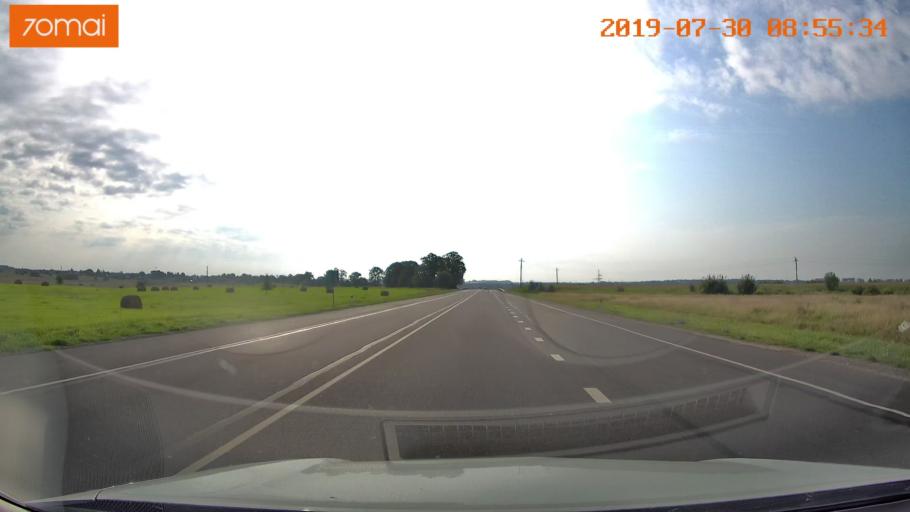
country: RU
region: Kaliningrad
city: Gusev
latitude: 54.6010
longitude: 22.0537
